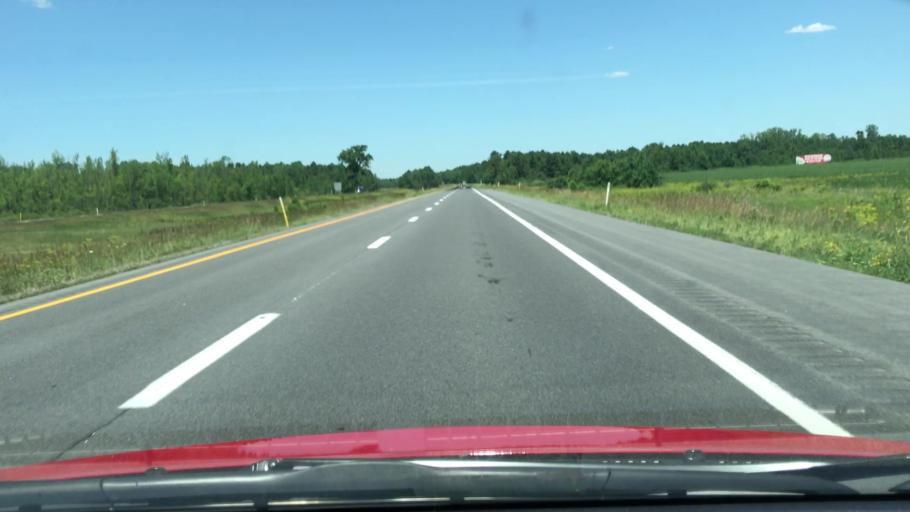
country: US
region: New York
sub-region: Clinton County
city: Cumberland Head
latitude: 44.8349
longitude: -73.4464
